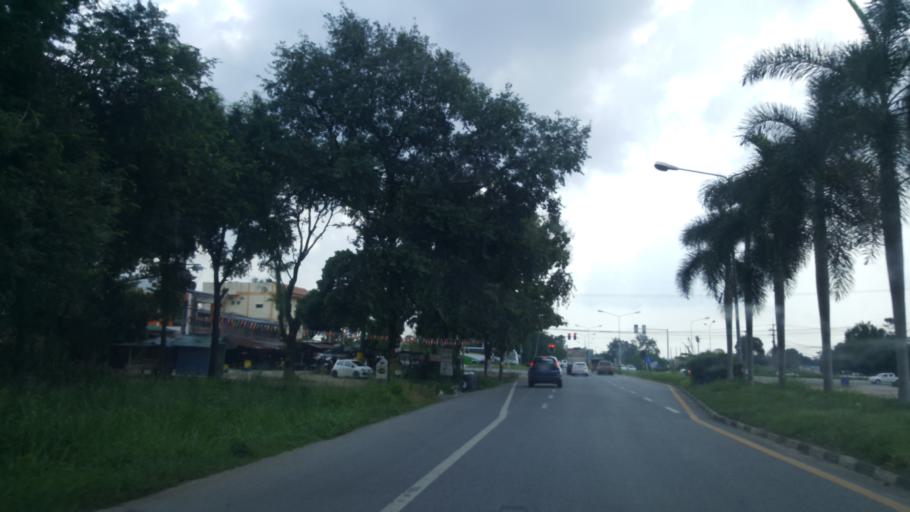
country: TH
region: Rayong
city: Ban Chang
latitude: 12.7266
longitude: 100.9809
